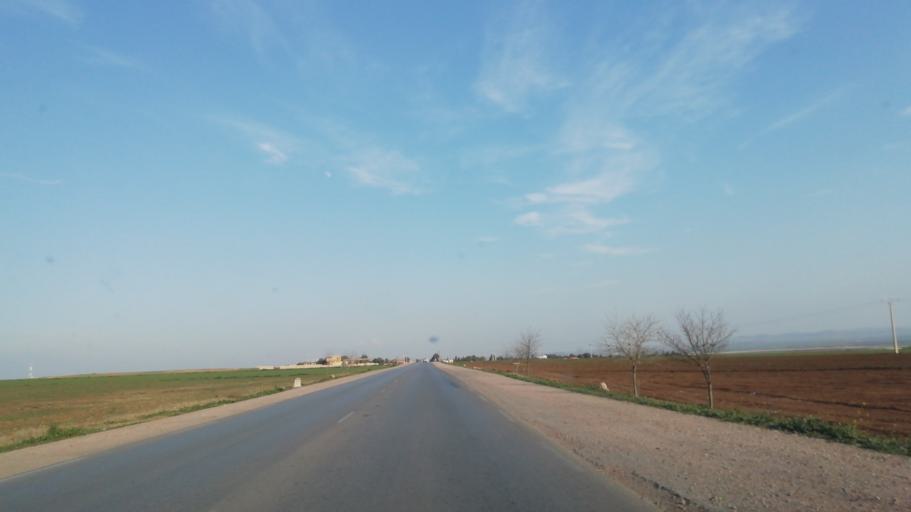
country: DZ
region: Relizane
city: Djidiouia
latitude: 35.8945
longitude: 0.6540
